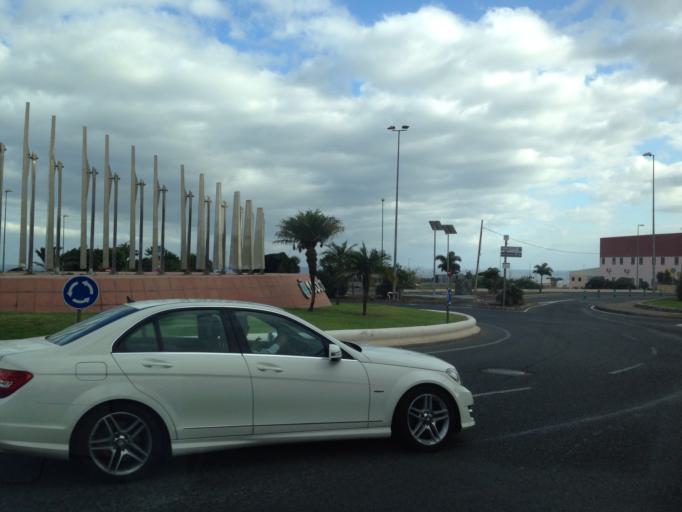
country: ES
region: Canary Islands
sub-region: Provincia de Las Palmas
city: Cruce de Arinaga
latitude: 27.8365
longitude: -15.4505
